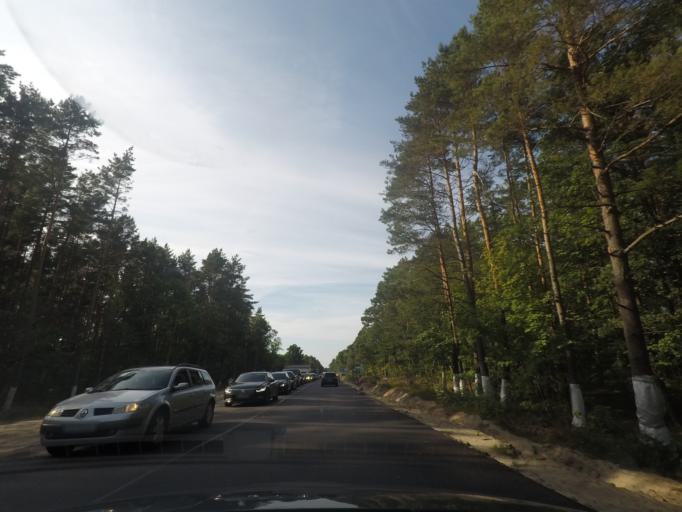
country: PL
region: Pomeranian Voivodeship
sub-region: Powiat leborski
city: Leba
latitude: 54.7114
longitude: 17.5795
